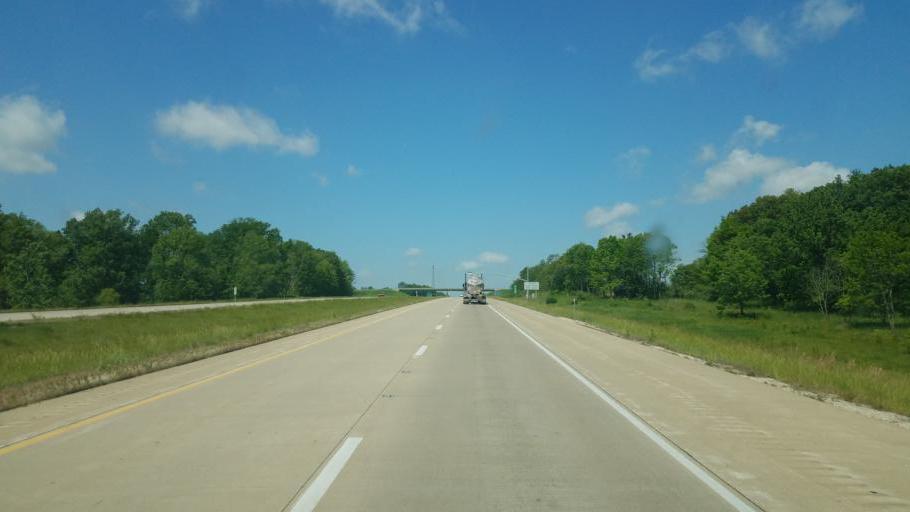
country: US
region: Illinois
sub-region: Clark County
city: Marshall
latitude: 39.4257
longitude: -87.5953
